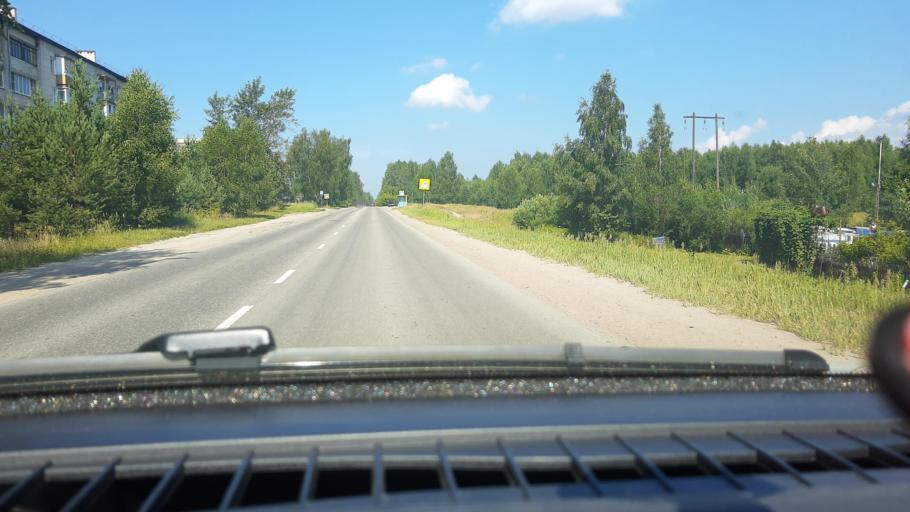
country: RU
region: Nizjnij Novgorod
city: Afonino
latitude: 56.3038
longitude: 44.1827
